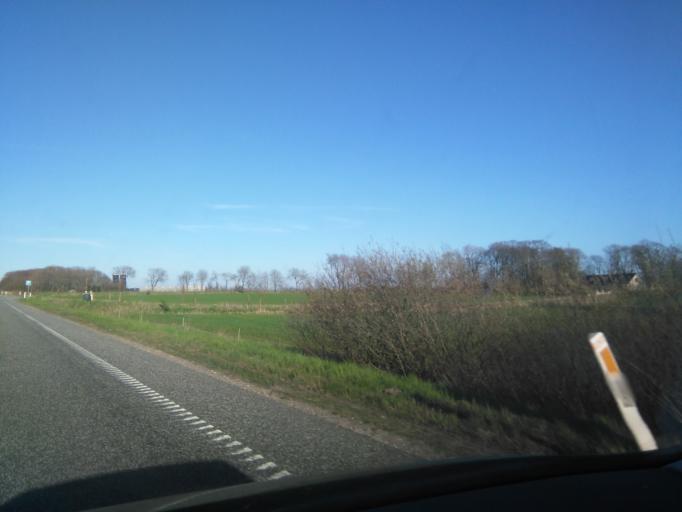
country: DK
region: Central Jutland
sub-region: Herning Kommune
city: Snejbjerg
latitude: 56.1240
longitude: 8.8351
